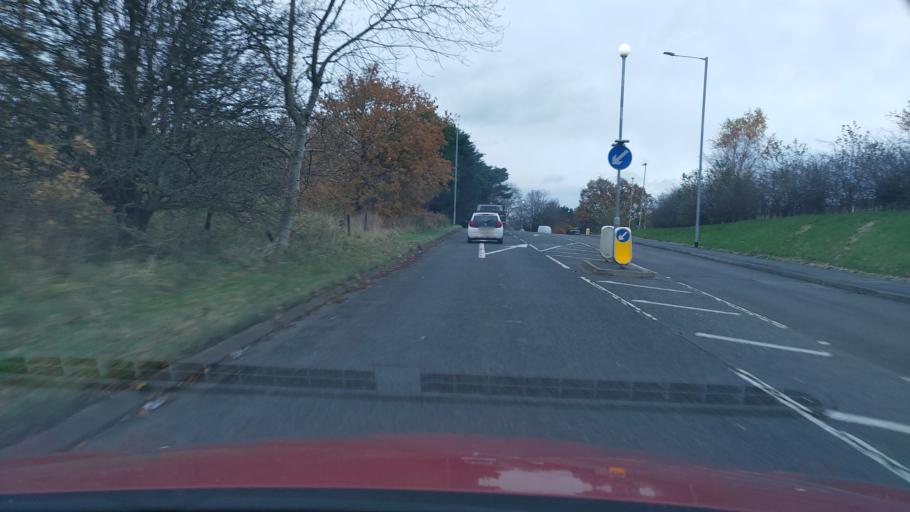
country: GB
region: England
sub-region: Lancashire
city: Euxton
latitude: 53.6808
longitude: -2.6764
